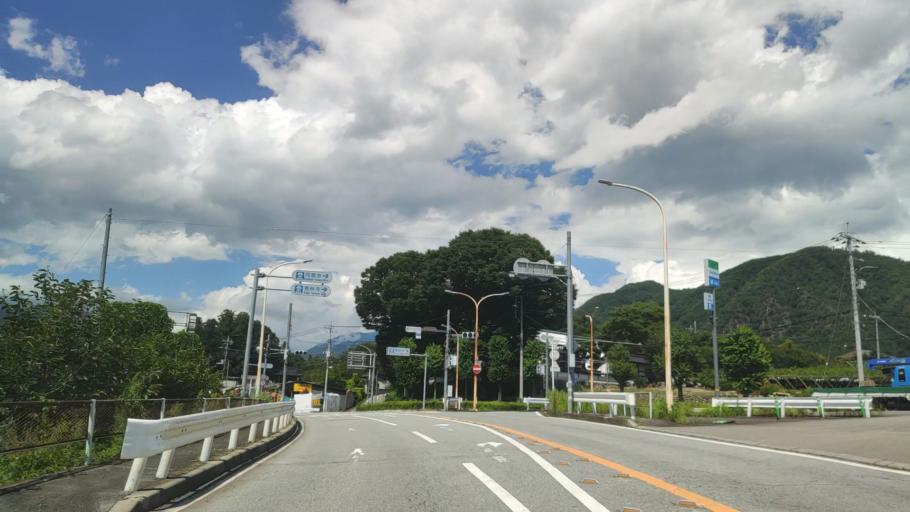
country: JP
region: Yamanashi
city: Enzan
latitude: 35.7313
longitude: 138.7117
